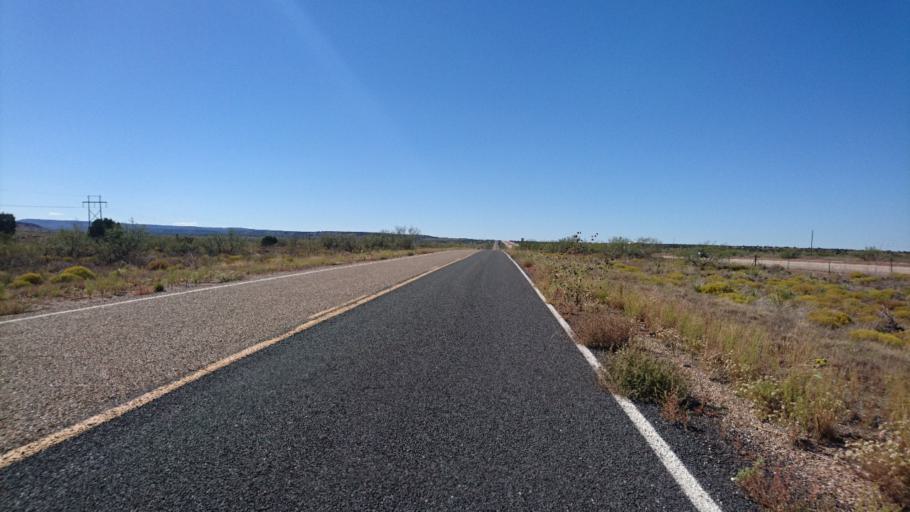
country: US
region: New Mexico
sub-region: Quay County
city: Tucumcari
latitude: 35.0775
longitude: -104.1329
